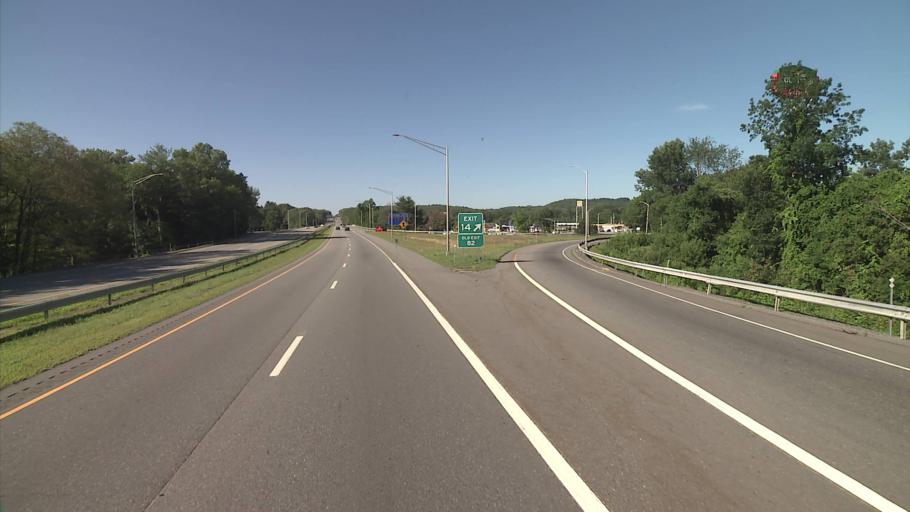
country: US
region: Connecticut
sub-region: New London County
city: Norwich
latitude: 41.5566
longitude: -72.1045
